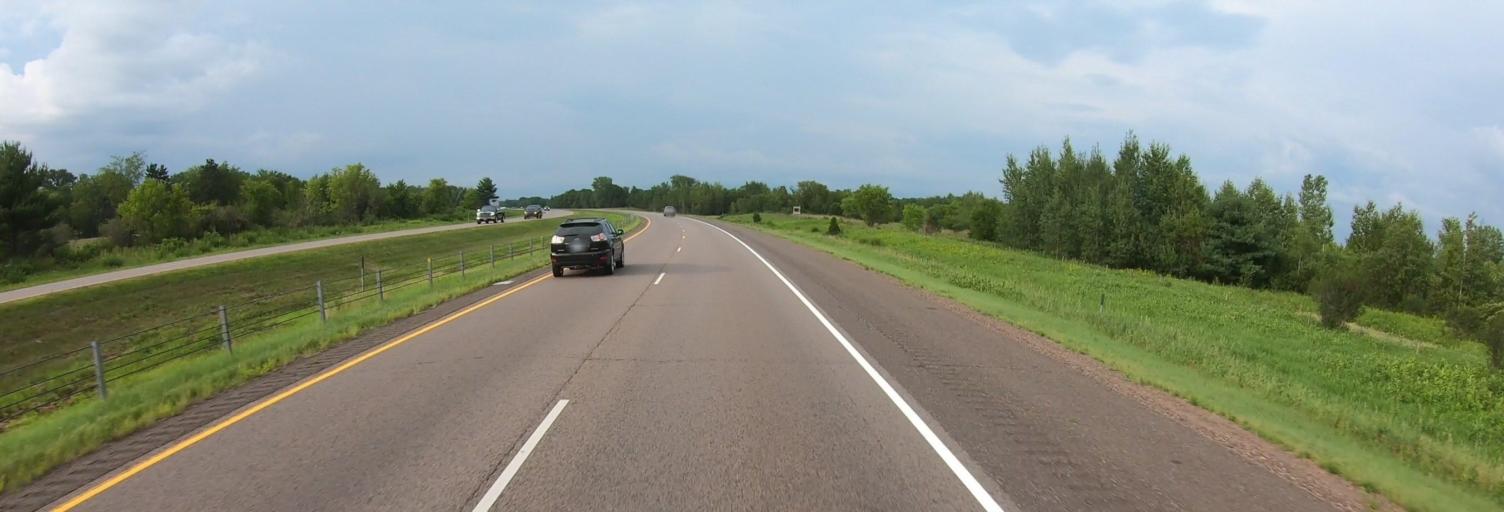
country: US
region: Minnesota
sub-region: Chisago County
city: Stacy
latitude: 45.4092
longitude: -92.9874
